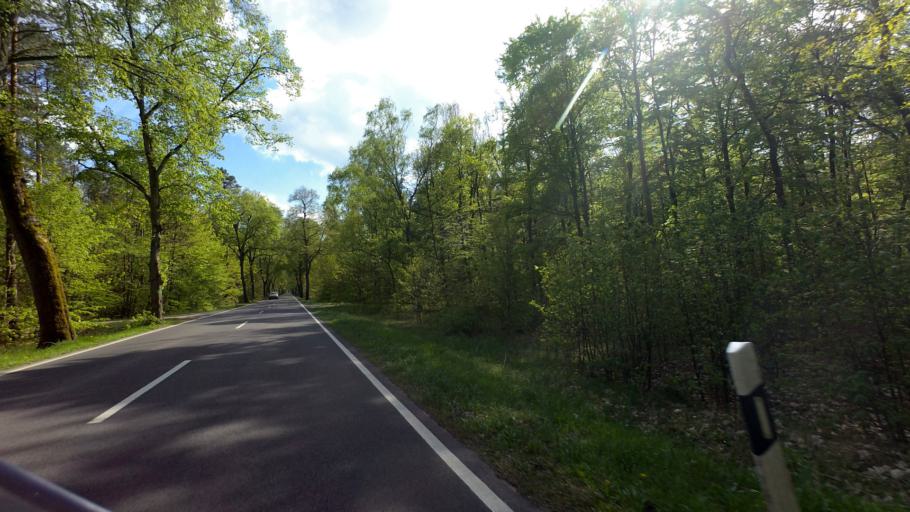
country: DE
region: Brandenburg
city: Milmersdorf
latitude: 53.0152
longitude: 13.6016
